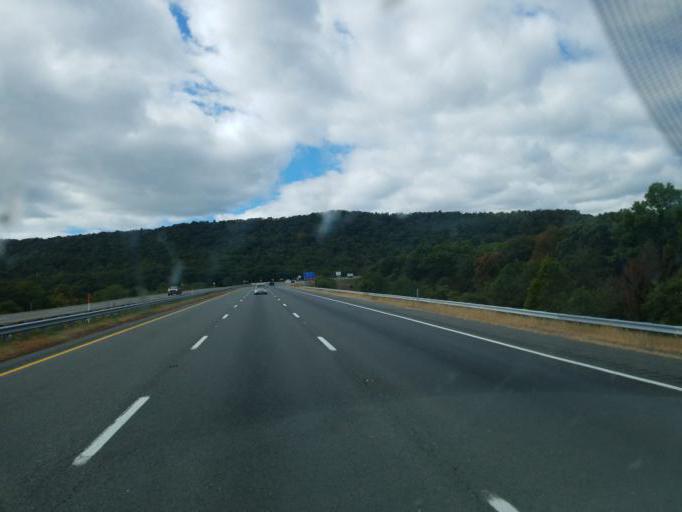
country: US
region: Maryland
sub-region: Washington County
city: Hancock
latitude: 39.7096
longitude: -78.2717
